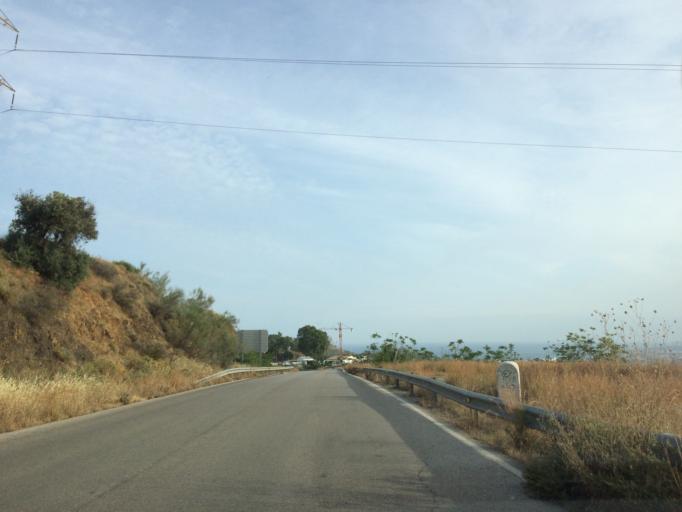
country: ES
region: Andalusia
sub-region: Provincia de Malaga
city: Malaga
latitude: 36.7521
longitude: -4.4082
